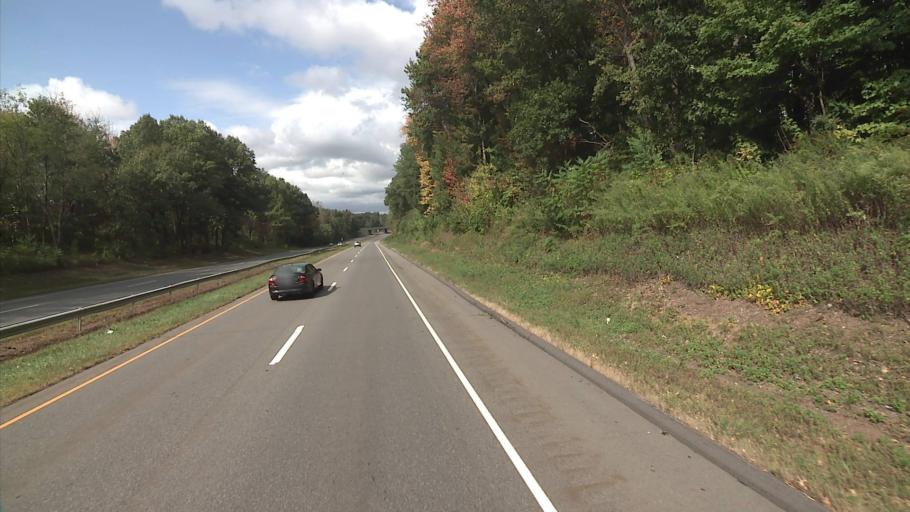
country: US
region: Connecticut
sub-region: New Haven County
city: Meriden
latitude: 41.5546
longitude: -72.7749
